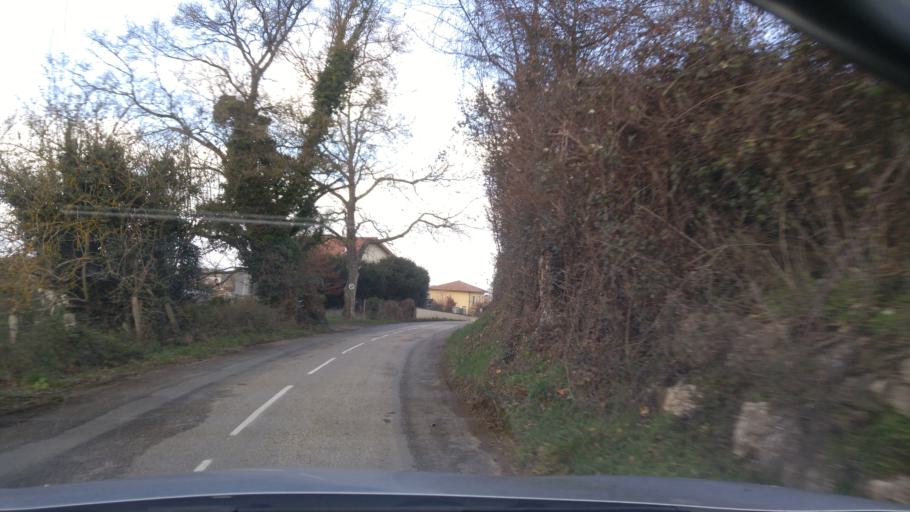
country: FR
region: Rhone-Alpes
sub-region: Departement de l'Isere
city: Roche
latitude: 45.5655
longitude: 5.1907
